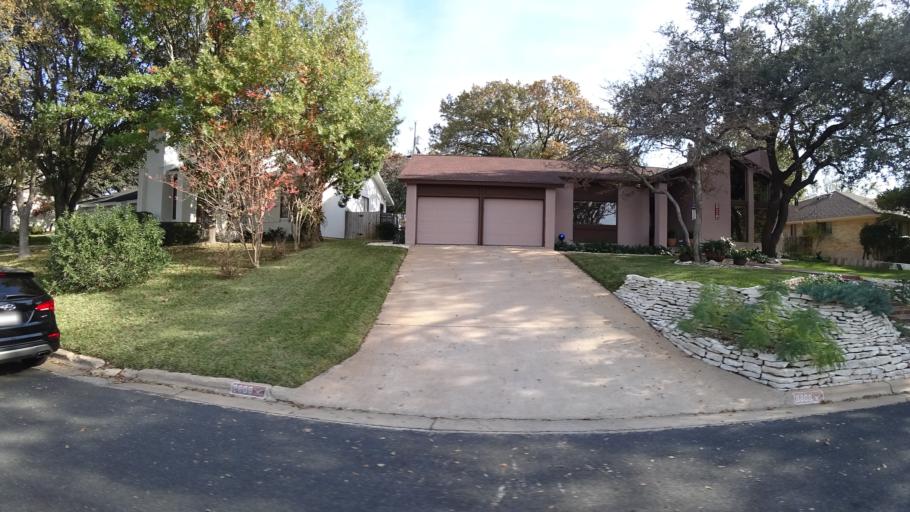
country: US
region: Texas
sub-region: Williamson County
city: Jollyville
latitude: 30.3859
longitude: -97.7574
